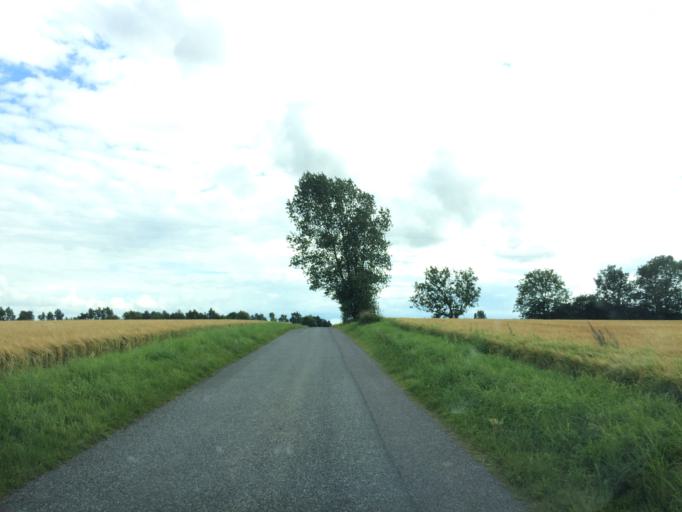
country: DK
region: South Denmark
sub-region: Odense Kommune
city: Bellinge
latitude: 55.2772
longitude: 10.3160
